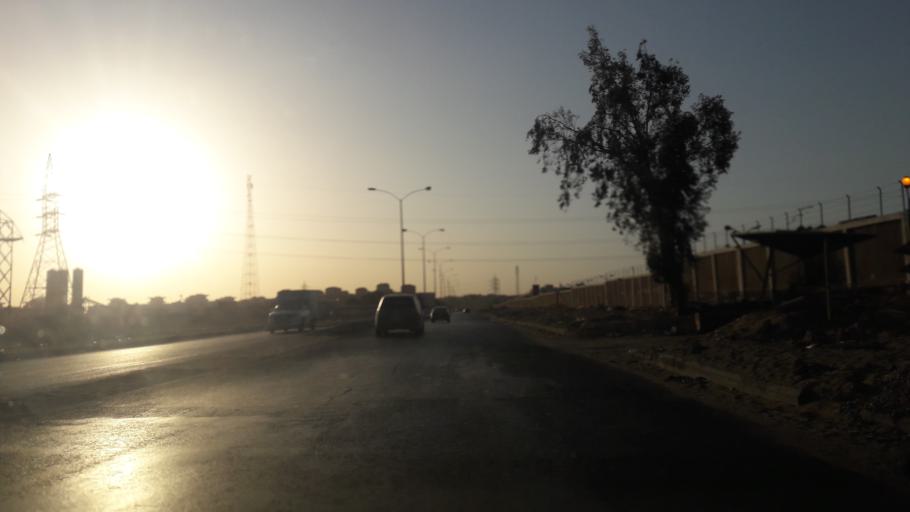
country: EG
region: Al Jizah
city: Madinat Sittah Uktubar
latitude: 29.9460
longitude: 30.9476
